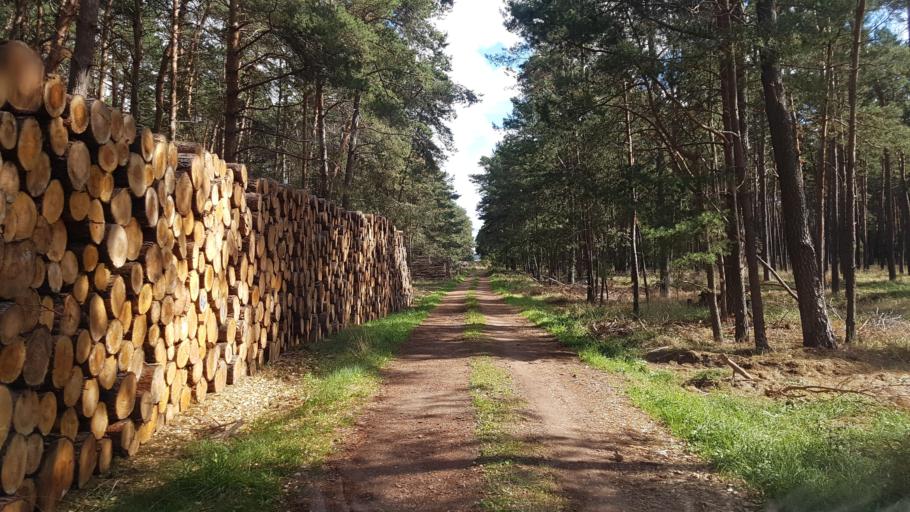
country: DE
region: Brandenburg
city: Niemegk
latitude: 52.0741
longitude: 12.7365
